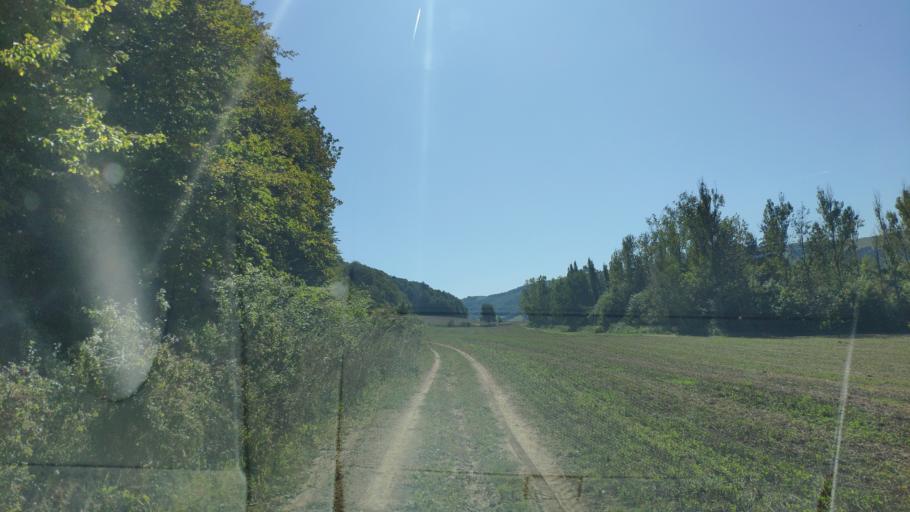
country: SK
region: Presovsky
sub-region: Okres Presov
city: Presov
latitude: 48.9786
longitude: 21.1399
